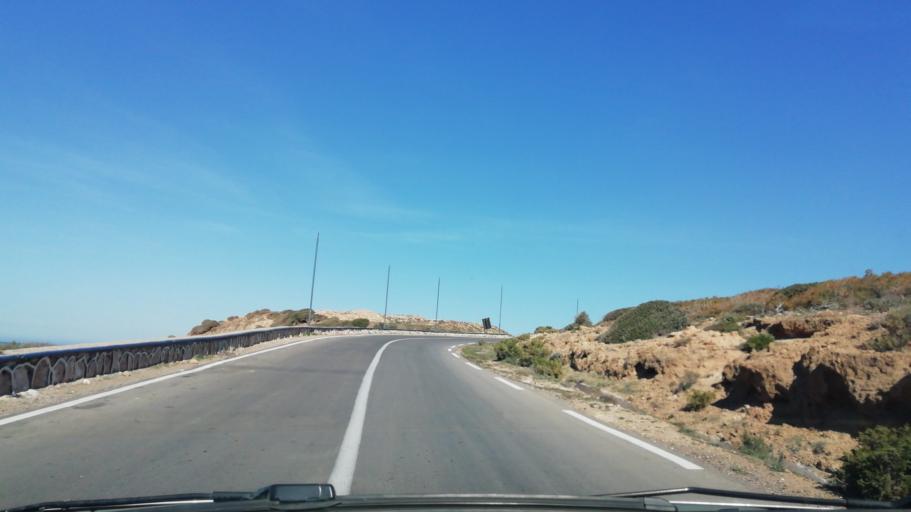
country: DZ
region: Ain Temouchent
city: El Amria
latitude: 35.6416
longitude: -1.0577
